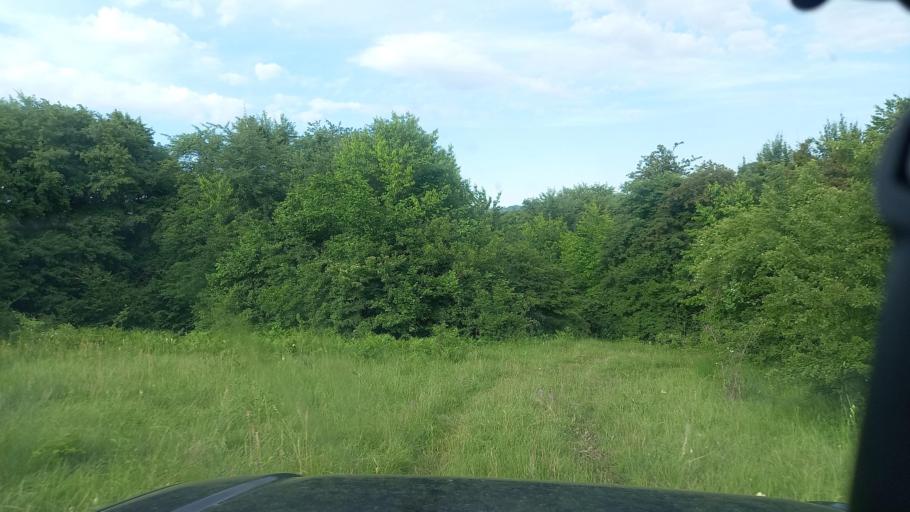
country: RU
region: Karachayevo-Cherkesiya
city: Kurdzhinovo
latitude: 44.1278
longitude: 41.0725
